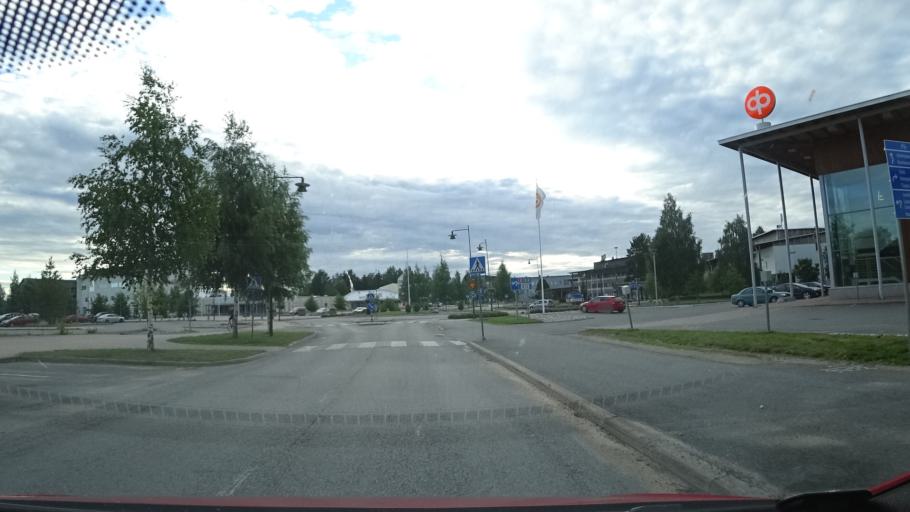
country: FI
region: Northern Ostrobothnia
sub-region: Oulu
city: Liminka
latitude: 64.8095
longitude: 25.4170
